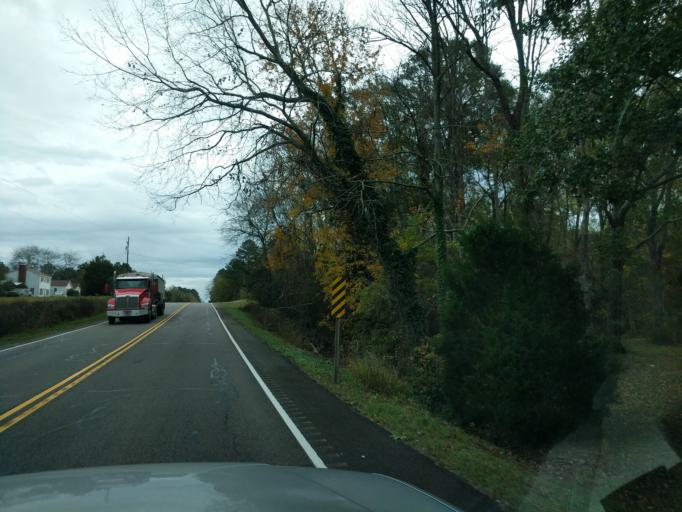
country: US
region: South Carolina
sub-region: Saluda County
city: Saluda
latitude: 33.9955
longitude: -81.7079
